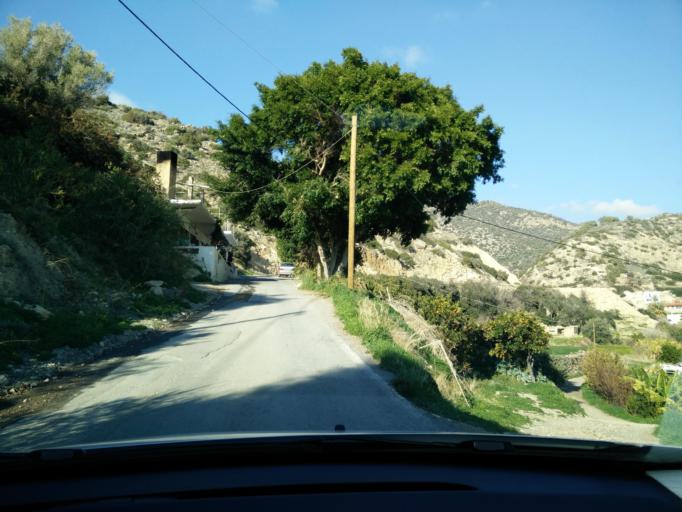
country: GR
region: Crete
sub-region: Nomos Lasithiou
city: Gra Liyia
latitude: 34.9927
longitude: 25.5321
